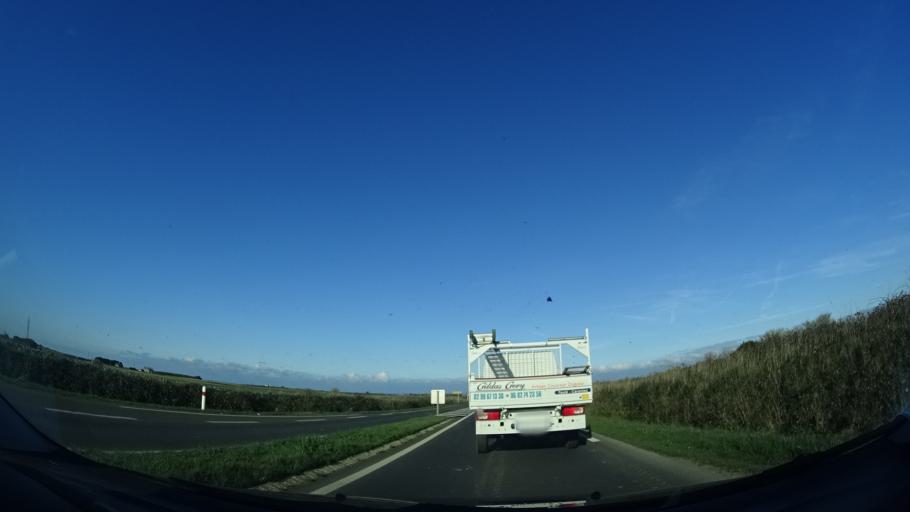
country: FR
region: Brittany
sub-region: Departement du Finistere
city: Saint-Pol-de-Leon
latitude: 48.6903
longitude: -3.9985
